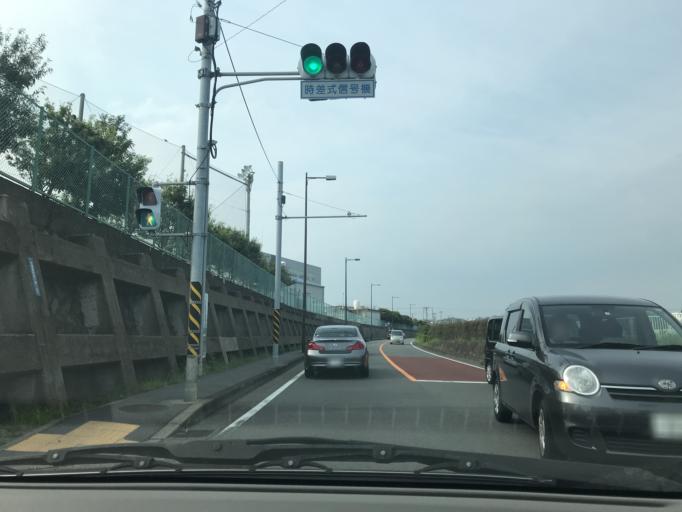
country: JP
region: Kanagawa
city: Fujisawa
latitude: 35.3397
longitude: 139.4675
